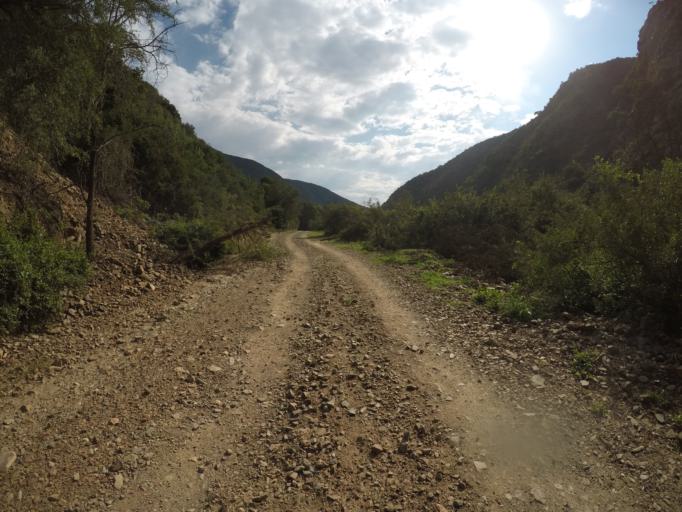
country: ZA
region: Eastern Cape
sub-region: Cacadu District Municipality
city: Kareedouw
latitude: -33.6424
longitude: 24.3145
